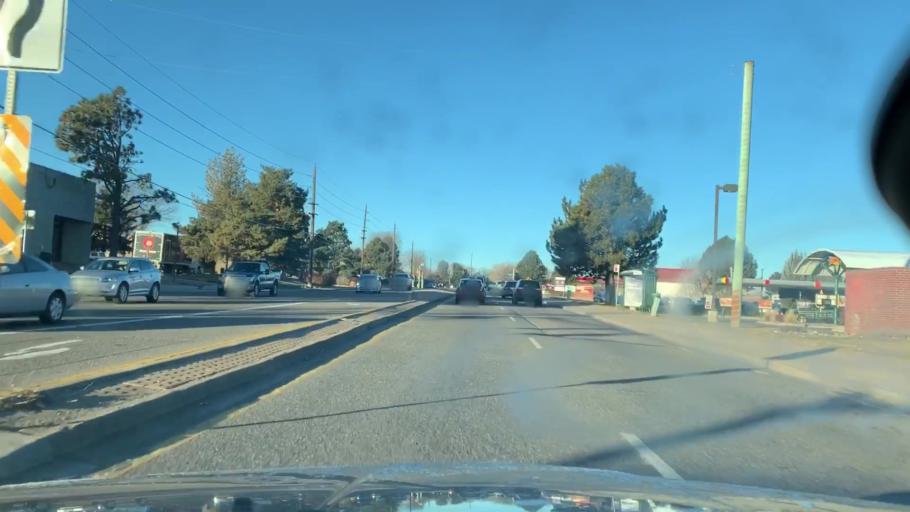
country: US
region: Colorado
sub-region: Arapahoe County
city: Glendale
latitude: 39.6749
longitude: -104.8970
